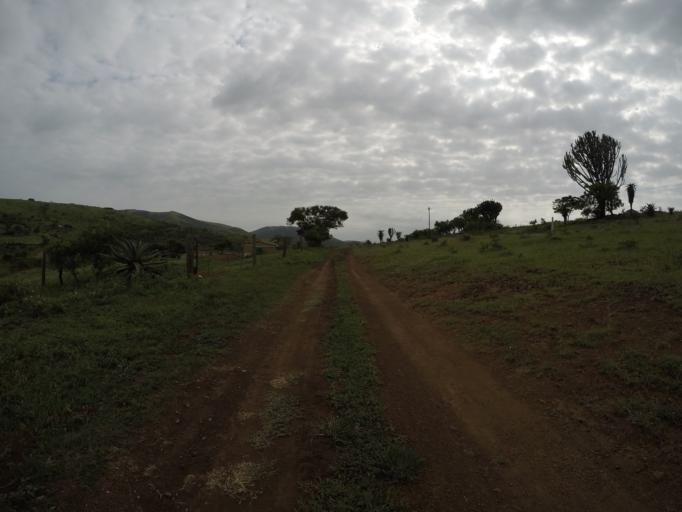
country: ZA
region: KwaZulu-Natal
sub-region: uThungulu District Municipality
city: Empangeni
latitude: -28.6301
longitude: 31.9059
